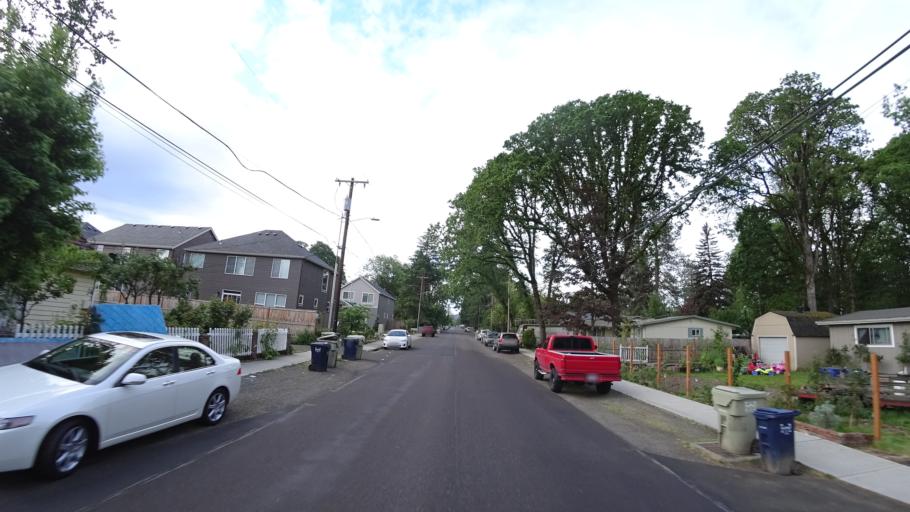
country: US
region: Oregon
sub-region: Washington County
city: Aloha
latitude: 45.4985
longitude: -122.8606
